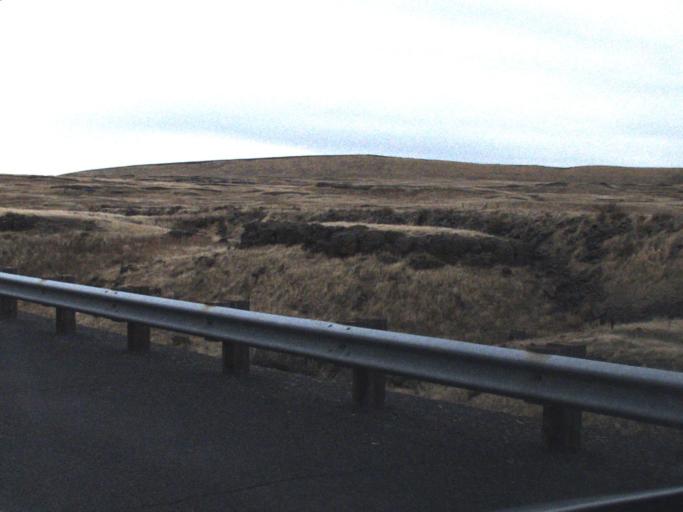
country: US
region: Washington
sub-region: Adams County
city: Ritzville
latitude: 46.7628
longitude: -118.1661
